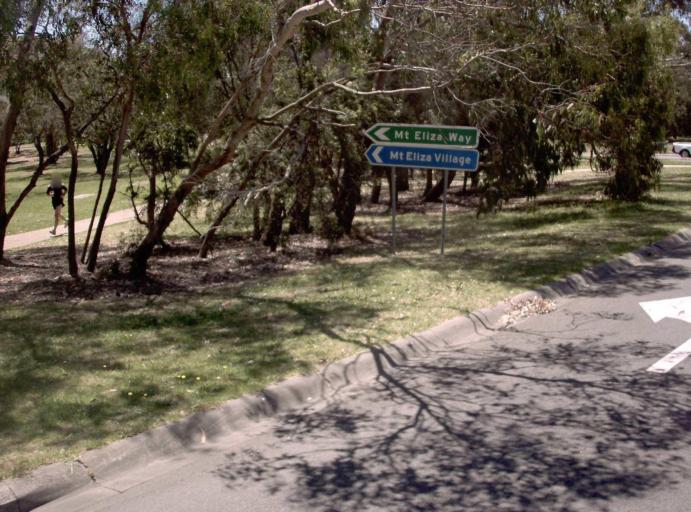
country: AU
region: Victoria
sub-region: Mornington Peninsula
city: Mount Eliza
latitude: -38.1952
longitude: 145.0907
